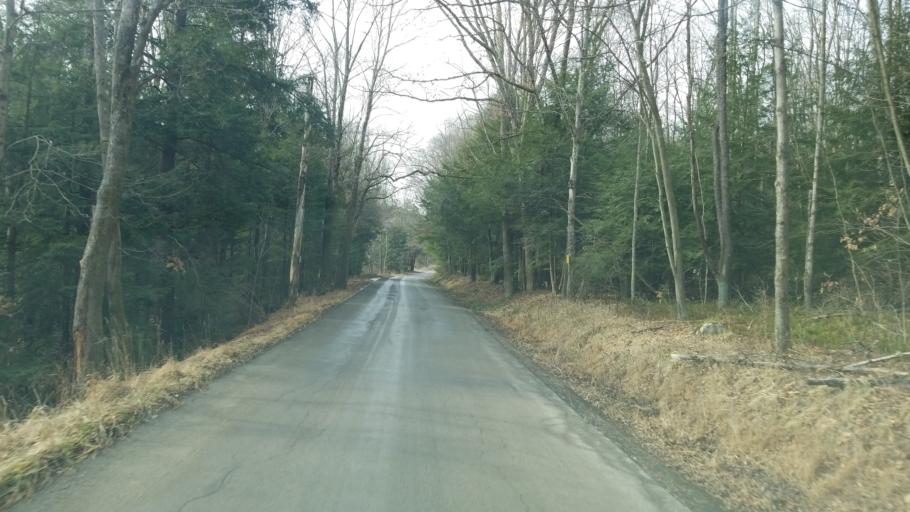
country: US
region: Pennsylvania
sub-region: Indiana County
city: Johnsonburg
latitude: 40.8293
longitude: -78.9307
